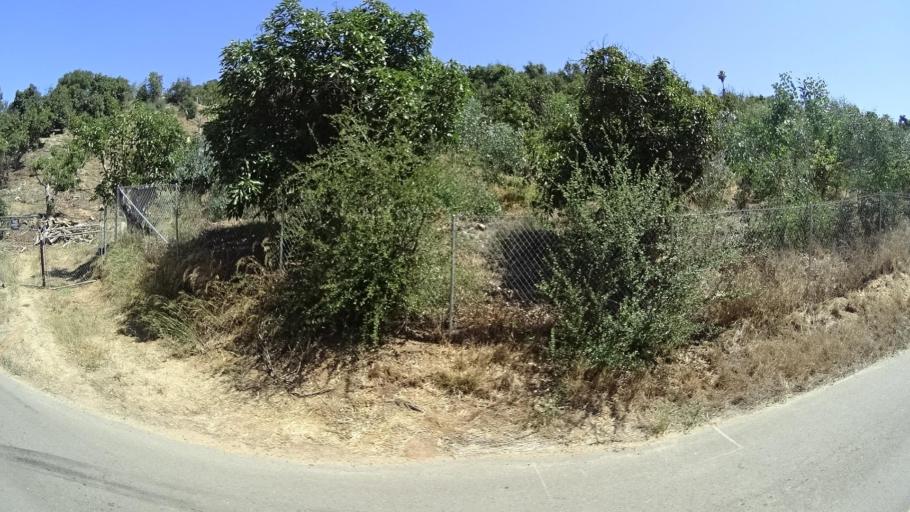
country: US
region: California
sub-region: San Diego County
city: Rainbow
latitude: 33.3890
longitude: -117.1410
